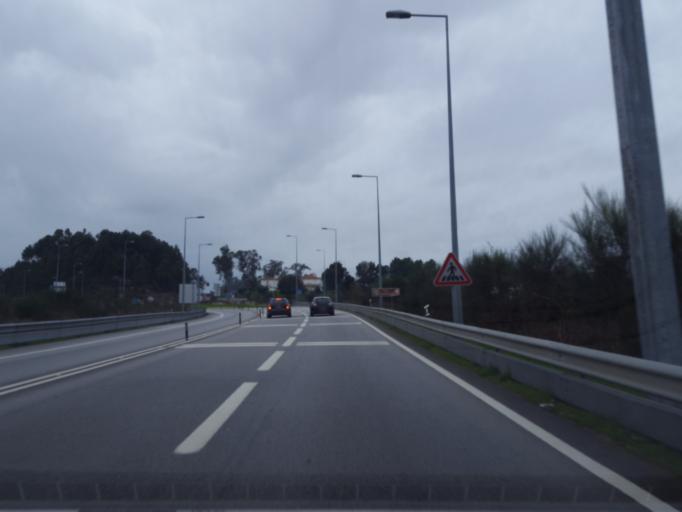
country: PT
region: Porto
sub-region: Lousada
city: Meinedo
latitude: 41.2355
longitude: -8.2000
